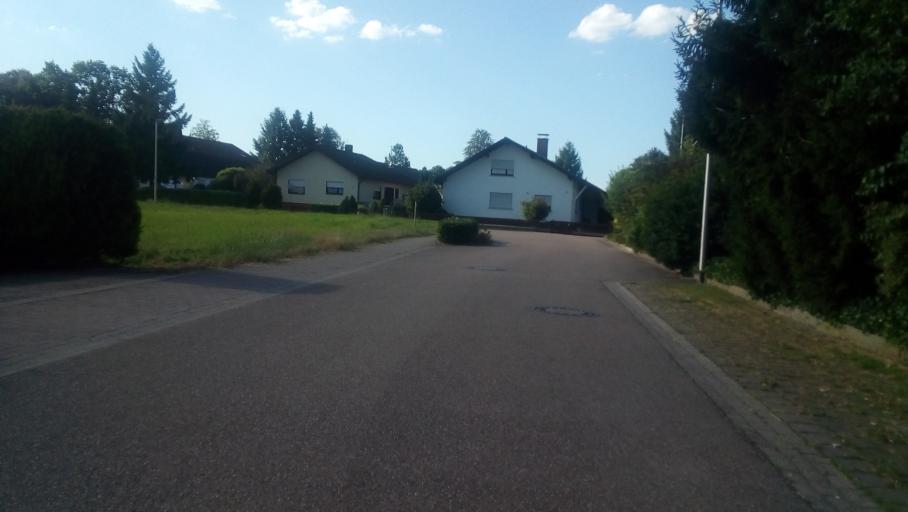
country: DE
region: Baden-Wuerttemberg
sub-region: Karlsruhe Region
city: Lichtenau
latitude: 48.7073
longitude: 7.9728
